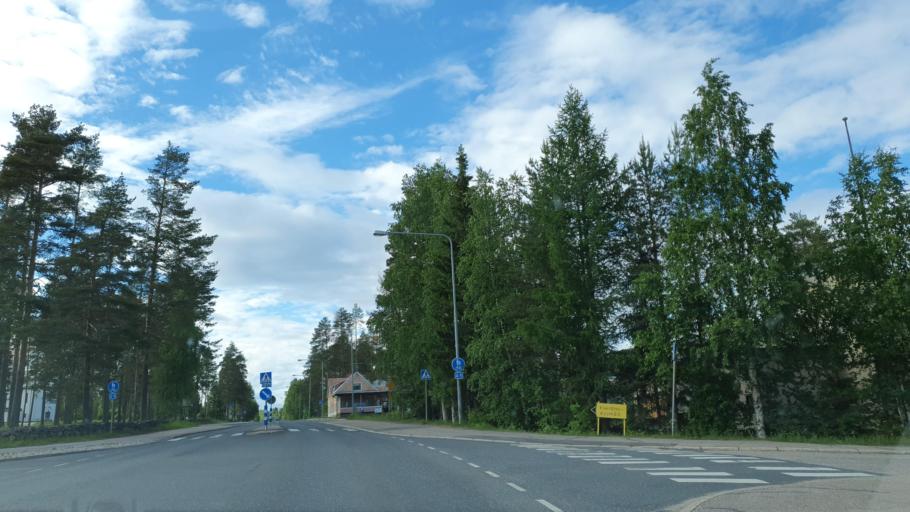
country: FI
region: Kainuu
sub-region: Kajaani
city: Paltamo
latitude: 64.4074
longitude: 27.8386
